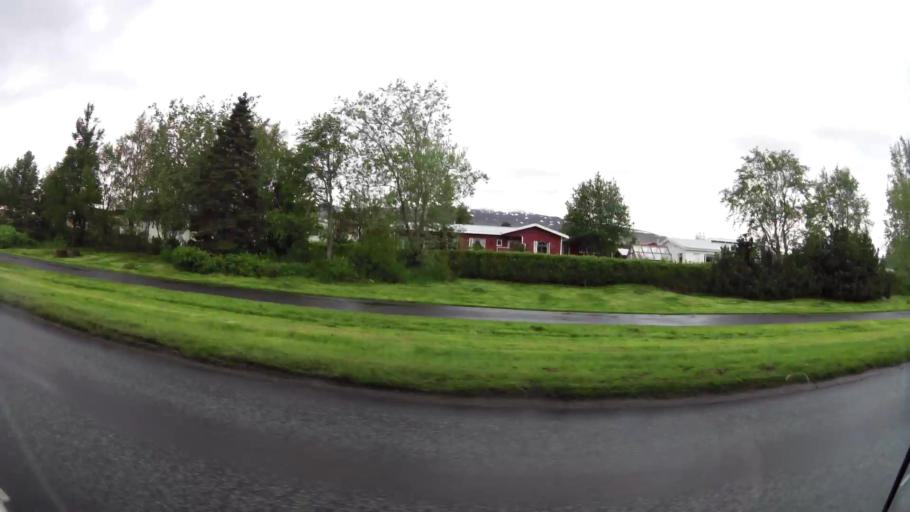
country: IS
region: Northeast
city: Akureyri
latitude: 65.6898
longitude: -18.1294
